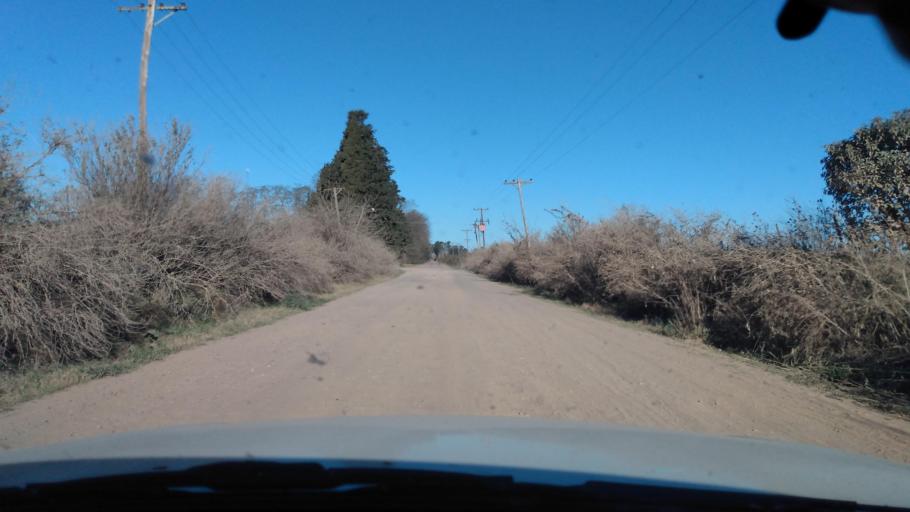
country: AR
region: Buenos Aires
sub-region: Partido de Mercedes
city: Mercedes
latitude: -34.6398
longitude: -59.3720
